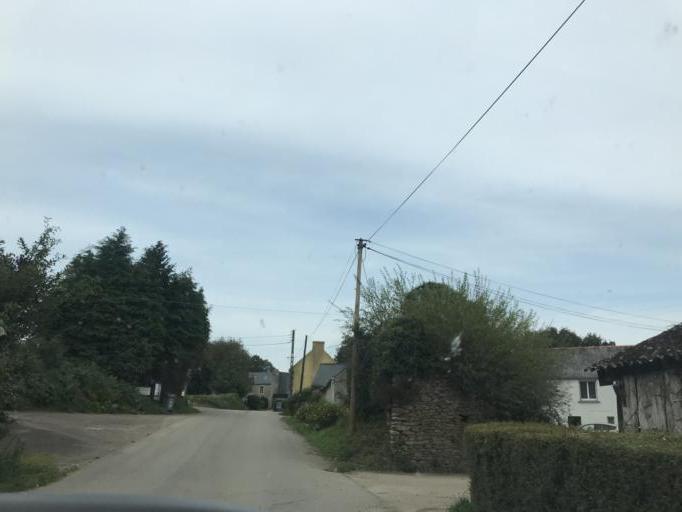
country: FR
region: Brittany
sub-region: Departement du Finistere
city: Plouneour-Menez
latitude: 48.3677
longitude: -3.8619
